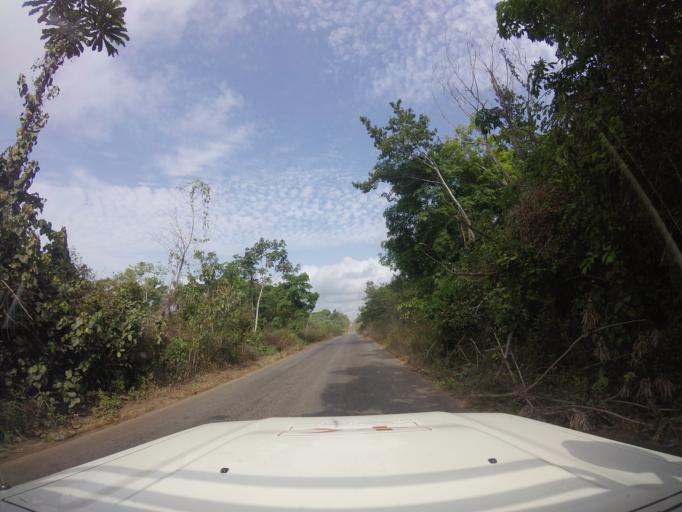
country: LR
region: Bomi
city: Tubmanburg
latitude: 6.6895
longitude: -10.8826
